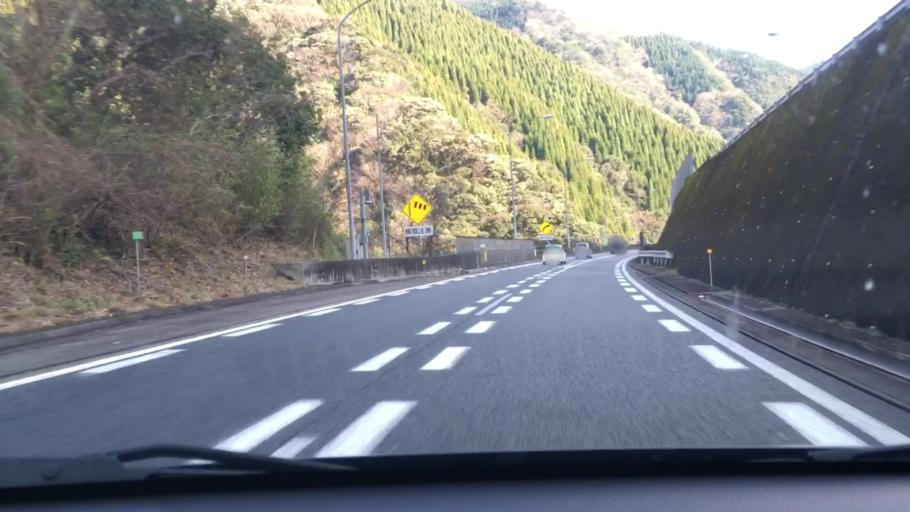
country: JP
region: Kumamoto
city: Hitoyoshi
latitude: 32.3271
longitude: 130.7547
